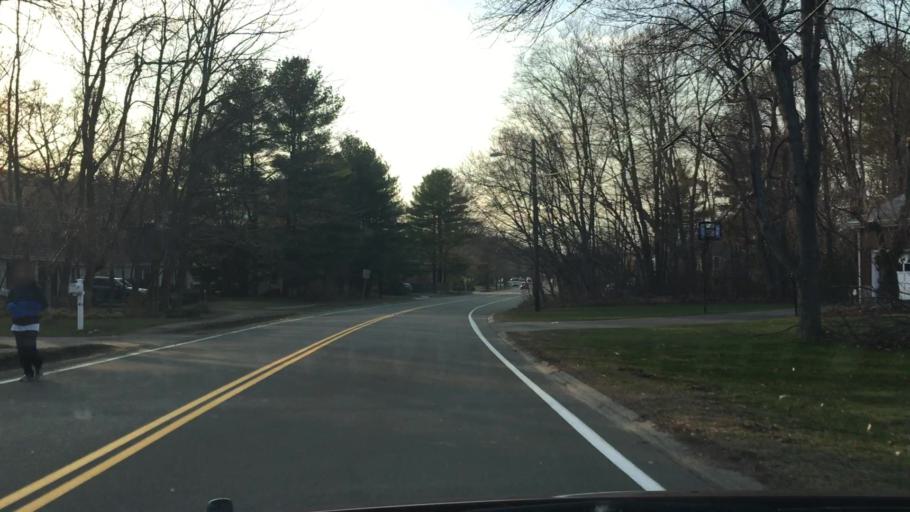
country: US
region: Massachusetts
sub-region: Middlesex County
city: Lexington
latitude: 42.4385
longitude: -71.2292
